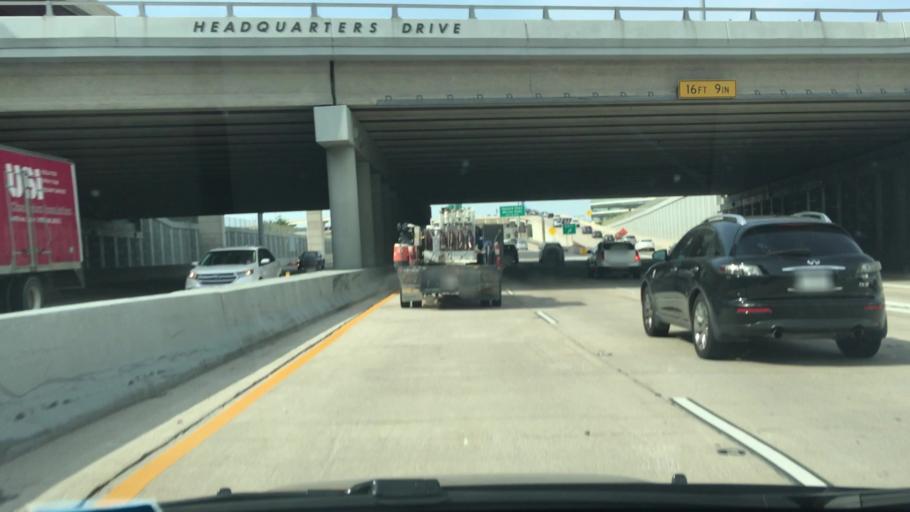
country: US
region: Texas
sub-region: Denton County
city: The Colony
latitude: 33.0833
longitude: -96.8236
